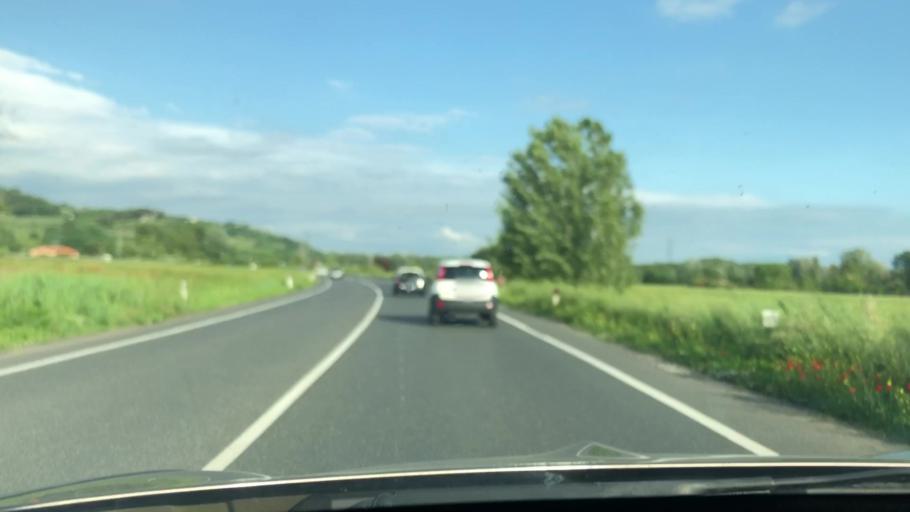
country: IT
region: Tuscany
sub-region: Province of Pisa
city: Treggiaia
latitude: 43.6195
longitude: 10.6677
